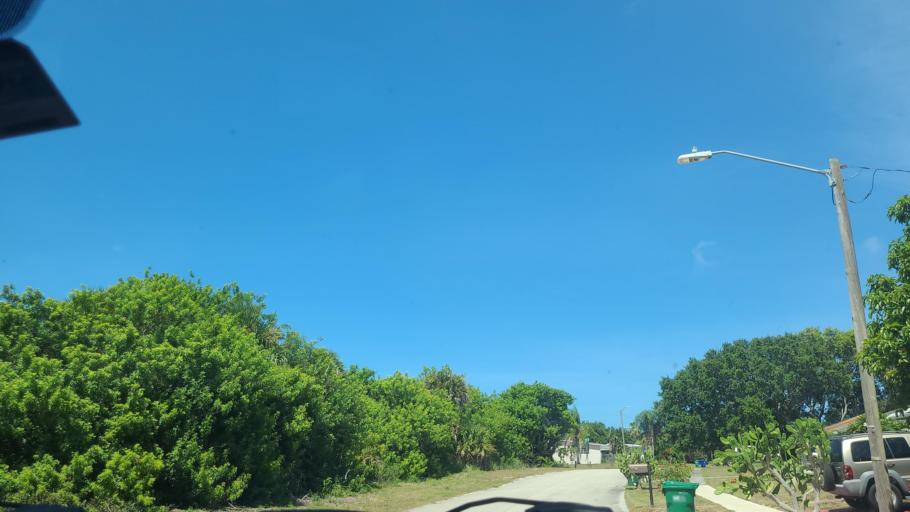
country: US
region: Florida
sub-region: Indian River County
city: Sebastian
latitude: 27.7883
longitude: -80.4626
